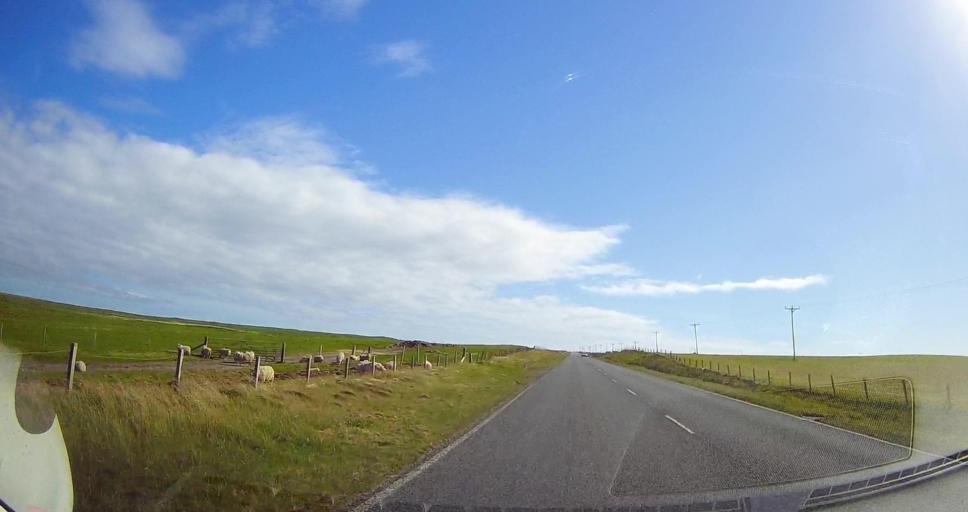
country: GB
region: Scotland
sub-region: Shetland Islands
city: Sandwick
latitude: 59.9060
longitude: -1.3023
